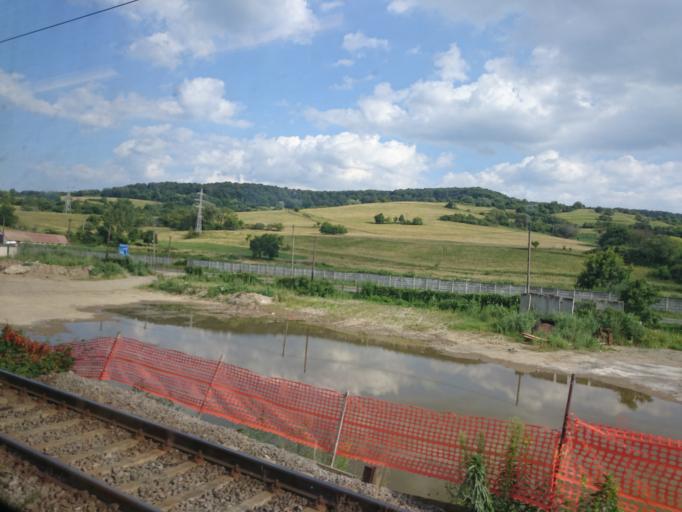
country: RO
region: Sibiu
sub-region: Oras Dumbraveni
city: Dumbraveni
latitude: 46.2159
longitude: 24.5630
